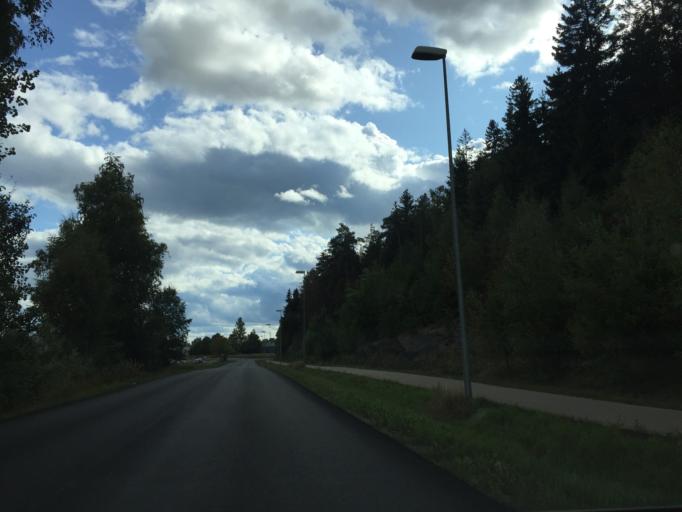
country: NO
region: Ostfold
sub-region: Askim
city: Askim
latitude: 59.5889
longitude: 11.1345
